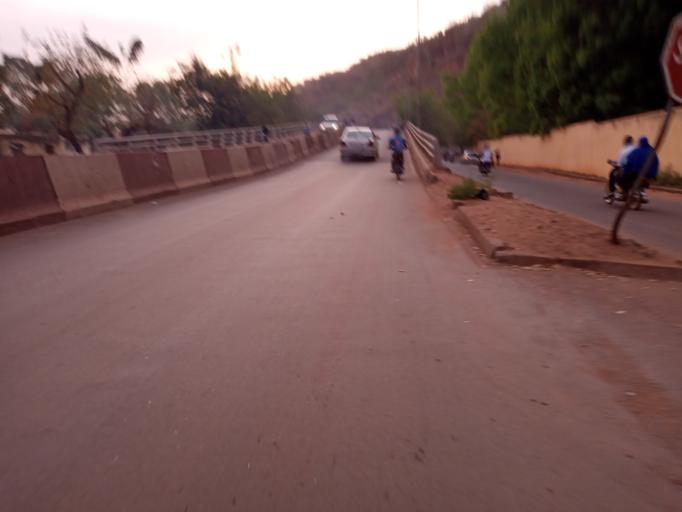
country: ML
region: Bamako
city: Bamako
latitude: 12.6577
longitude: -7.9990
